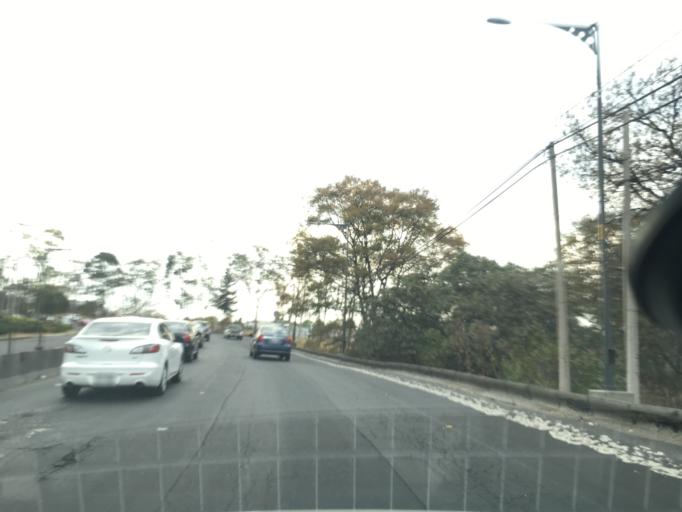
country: MX
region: Mexico City
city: Col. Bosques de las Lomas
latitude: 19.3736
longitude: -99.2687
